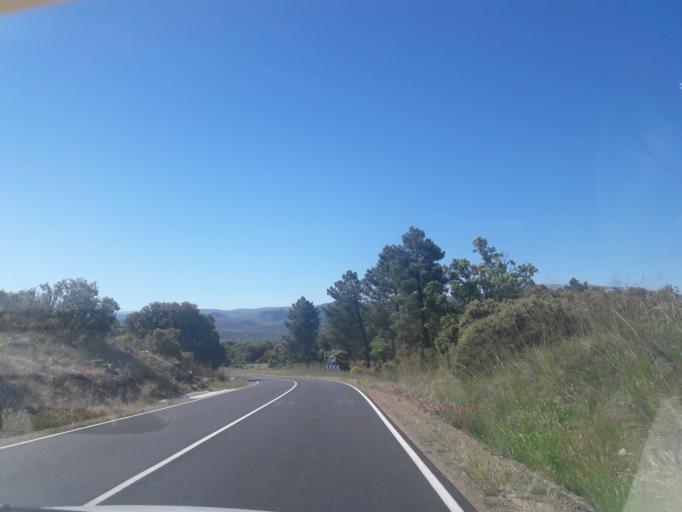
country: ES
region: Castille and Leon
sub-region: Provincia de Salamanca
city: Nava de Bejar
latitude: 40.4897
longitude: -5.6560
